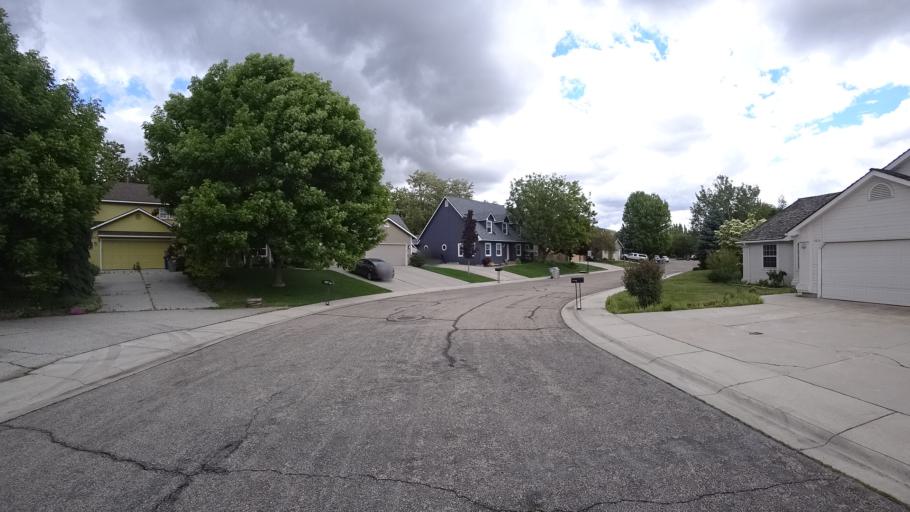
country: US
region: Idaho
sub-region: Ada County
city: Garden City
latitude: 43.6729
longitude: -116.2627
